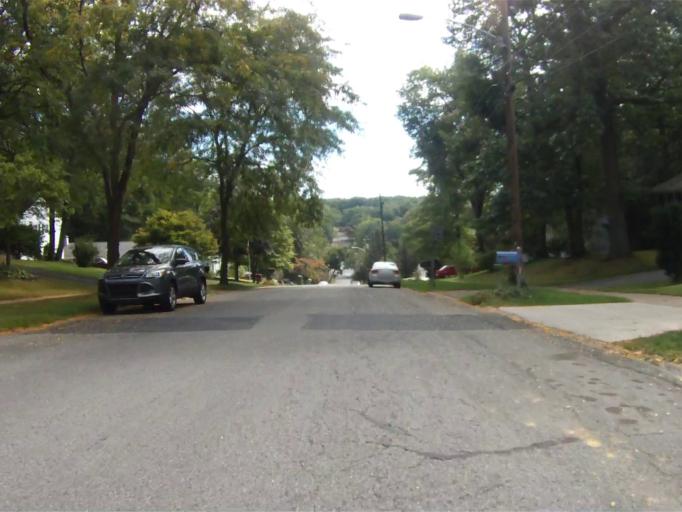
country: US
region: Pennsylvania
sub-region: Centre County
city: Park Forest Village
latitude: 40.8090
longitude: -77.9194
